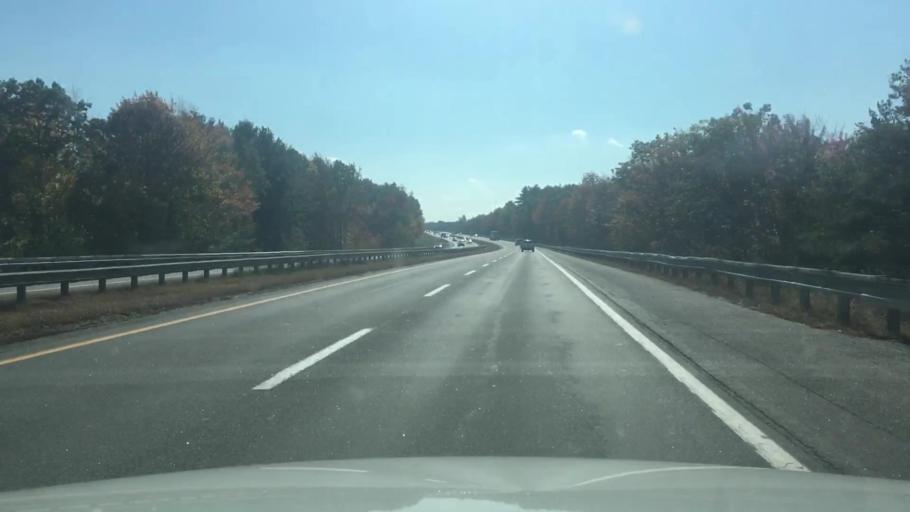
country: US
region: Maine
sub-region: Cumberland County
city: Westbrook
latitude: 43.6987
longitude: -70.3167
